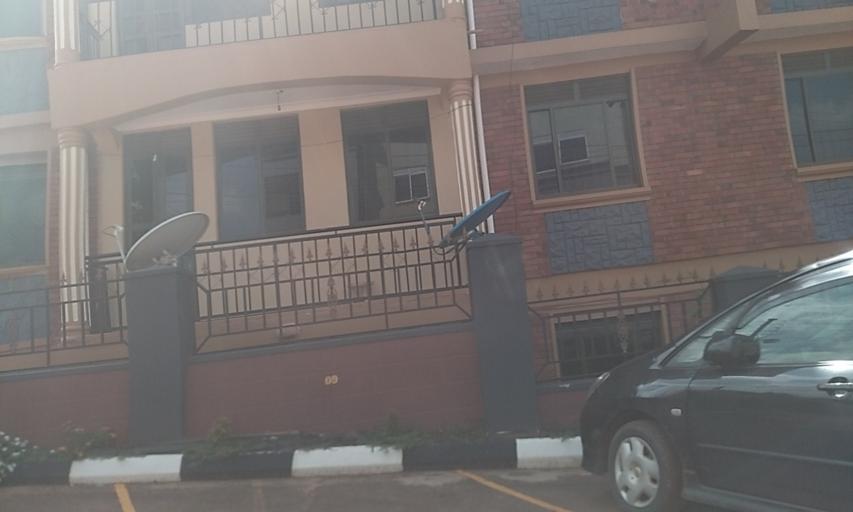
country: UG
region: Central Region
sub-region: Wakiso District
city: Kireka
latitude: 0.3484
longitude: 32.6156
